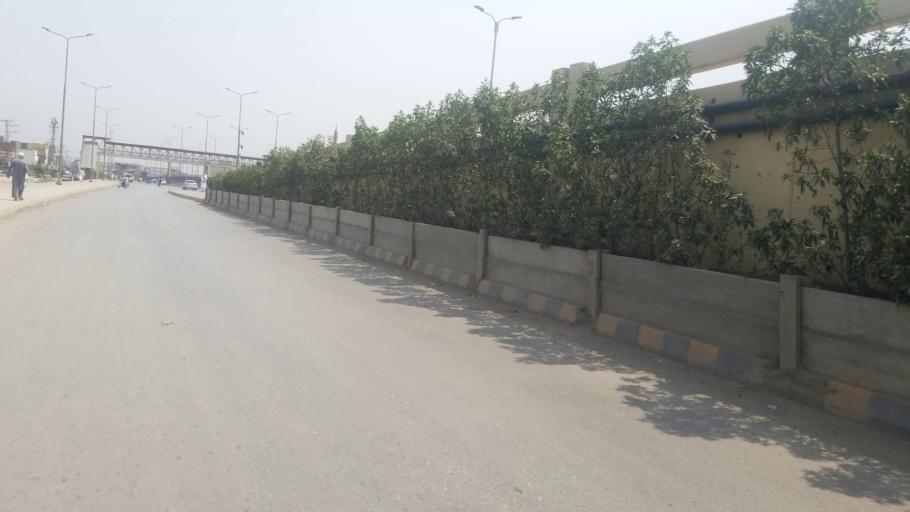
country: PK
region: Khyber Pakhtunkhwa
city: Peshawar
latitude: 34.0174
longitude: 71.6242
